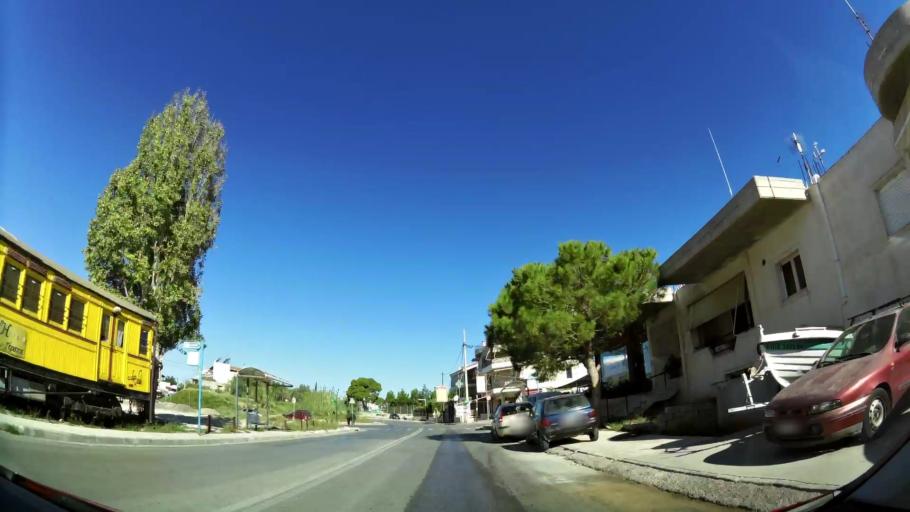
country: GR
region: Attica
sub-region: Nomarchia Anatolikis Attikis
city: Gerakas
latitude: 38.0205
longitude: 23.8507
